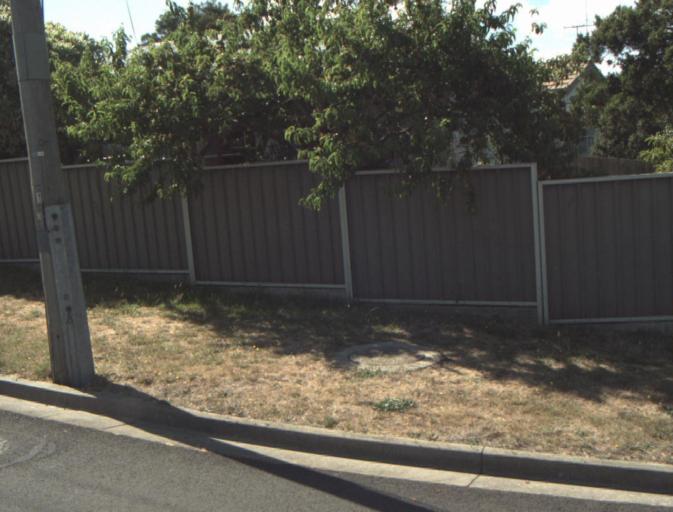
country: AU
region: Tasmania
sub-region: Launceston
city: Newstead
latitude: -41.4278
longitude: 147.1758
